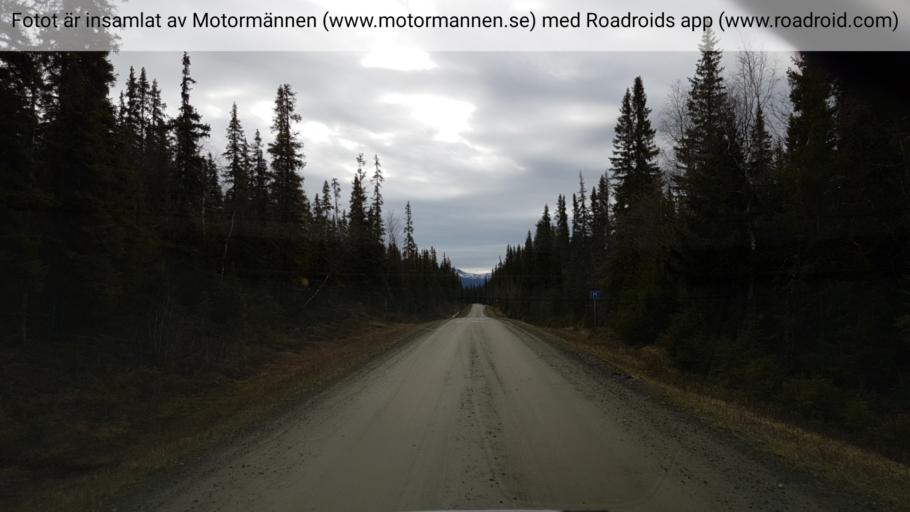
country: SE
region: Vaesterbotten
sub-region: Vilhelmina Kommun
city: Sjoberg
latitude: 65.5239
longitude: 15.4429
